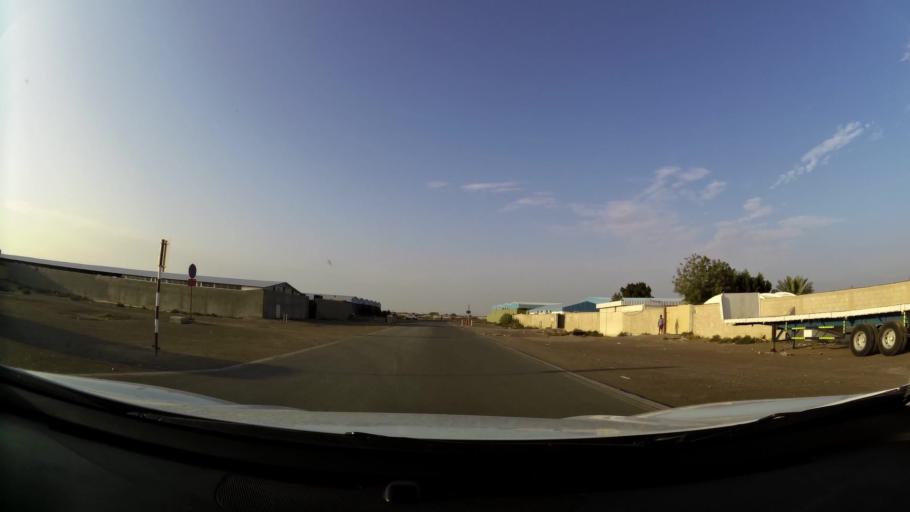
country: AE
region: Abu Dhabi
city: Al Ain
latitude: 24.1526
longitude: 55.8397
